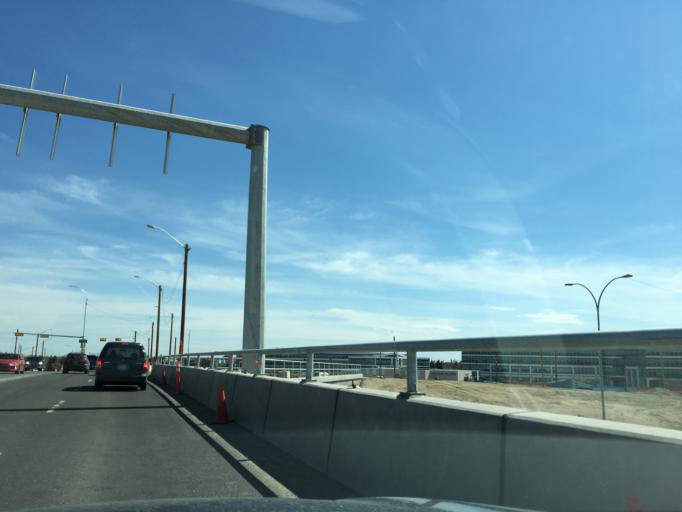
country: CA
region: Alberta
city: Calgary
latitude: 50.9047
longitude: -114.0622
